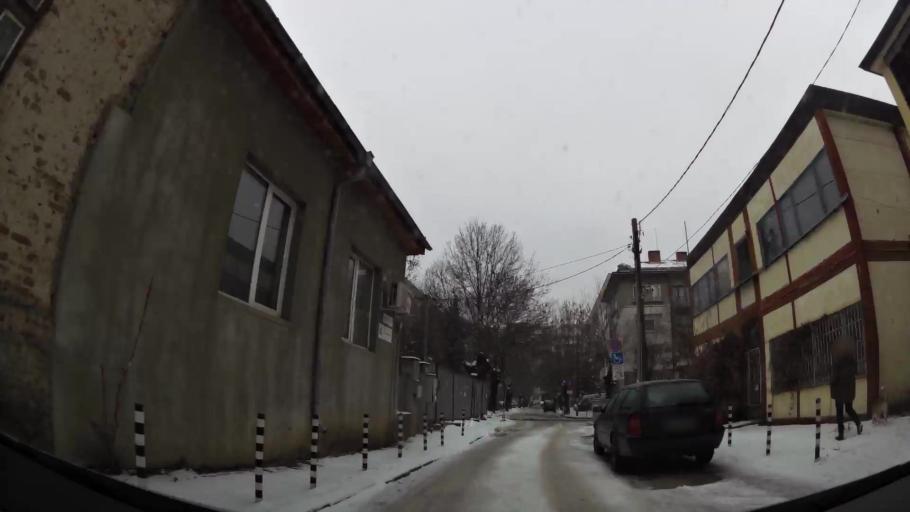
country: BG
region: Sofia-Capital
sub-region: Stolichna Obshtina
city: Sofia
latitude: 42.7114
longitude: 23.3170
